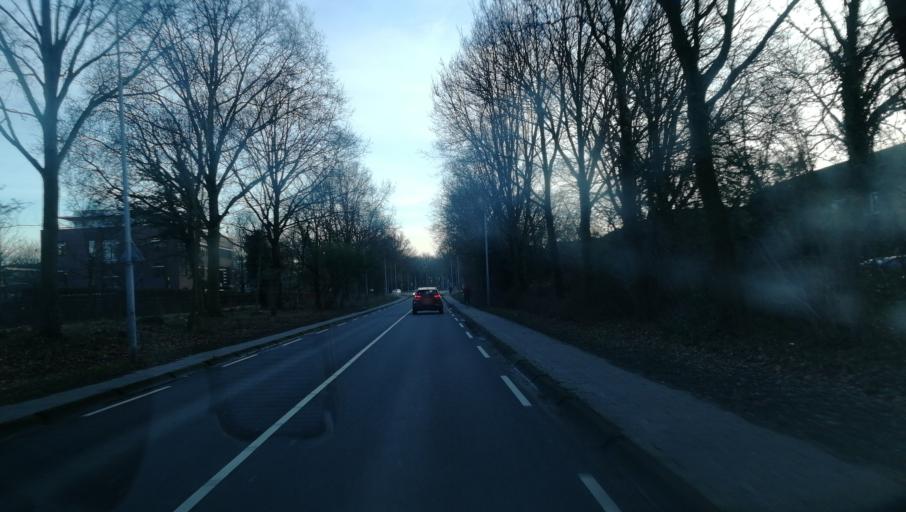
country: NL
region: Limburg
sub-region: Gemeente Venlo
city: Tegelen
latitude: 51.3697
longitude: 6.1359
